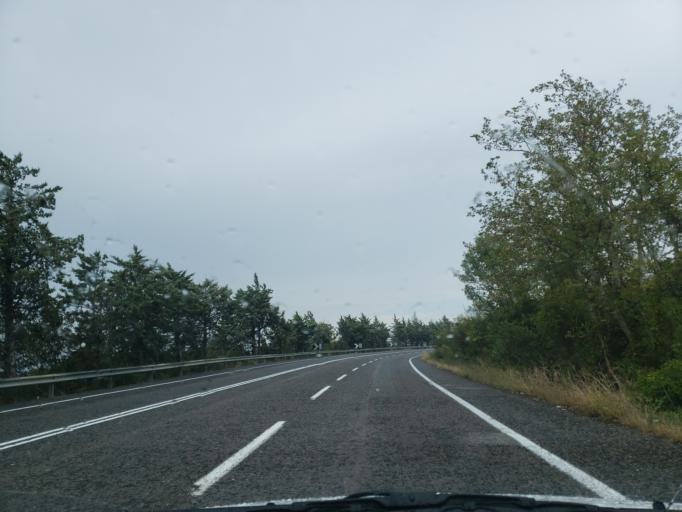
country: GR
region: Central Greece
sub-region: Nomos Fthiotidos
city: Anthili
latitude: 38.7903
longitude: 22.4879
